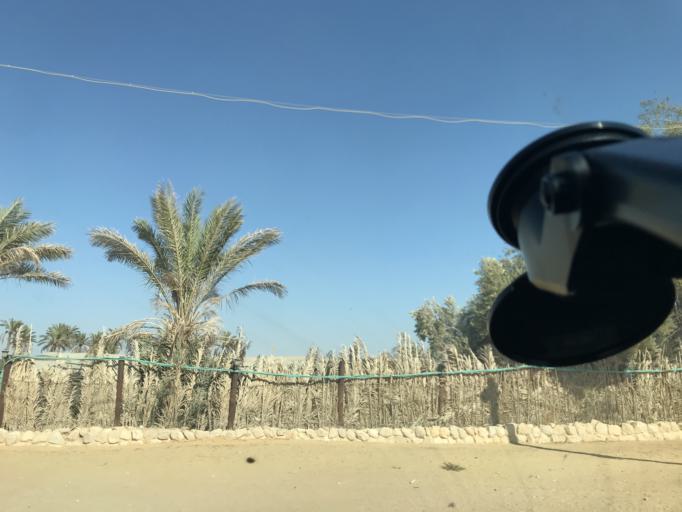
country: IL
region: Southern District
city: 'Arad
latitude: 31.3054
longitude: 35.2687
